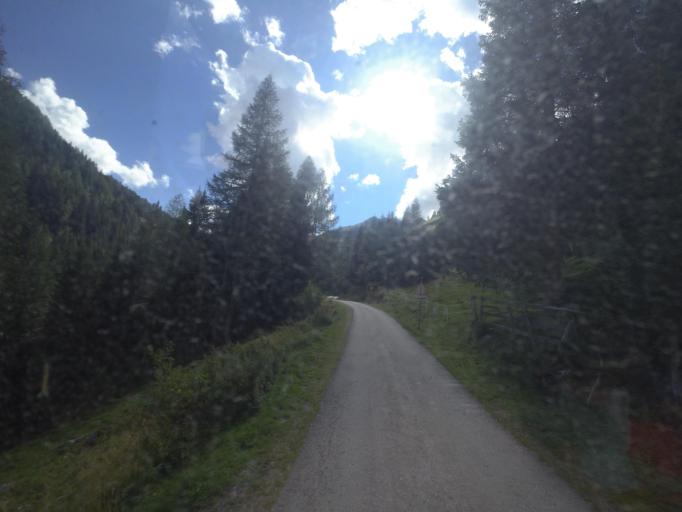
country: AT
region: Salzburg
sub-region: Politischer Bezirk Sankt Johann im Pongau
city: Kleinarl
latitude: 47.1862
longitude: 13.3632
